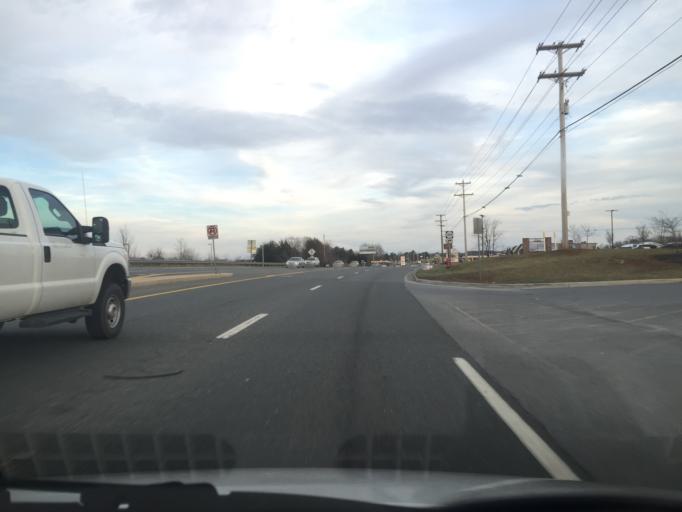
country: US
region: Virginia
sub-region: Bedford County
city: Forest
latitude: 37.3701
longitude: -79.3017
